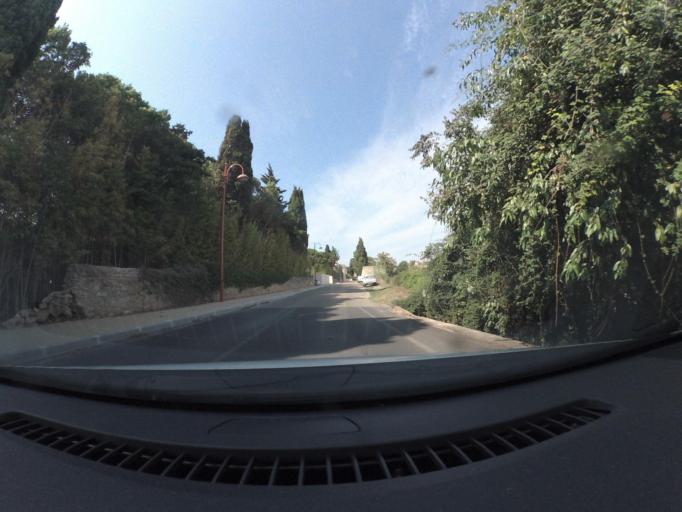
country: FR
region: Languedoc-Roussillon
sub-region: Departement de l'Herault
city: Baillargues
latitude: 43.6567
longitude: 4.0131
